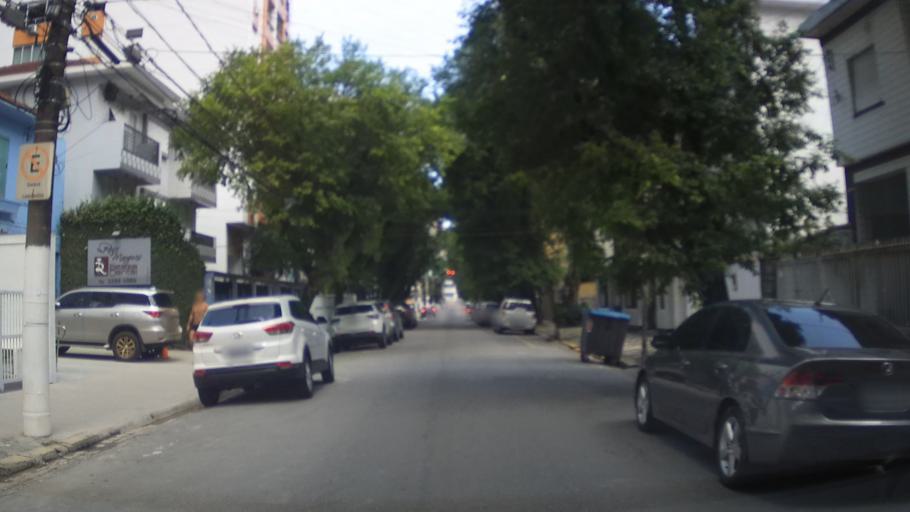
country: BR
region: Sao Paulo
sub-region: Santos
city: Santos
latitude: -23.9645
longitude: -46.3375
